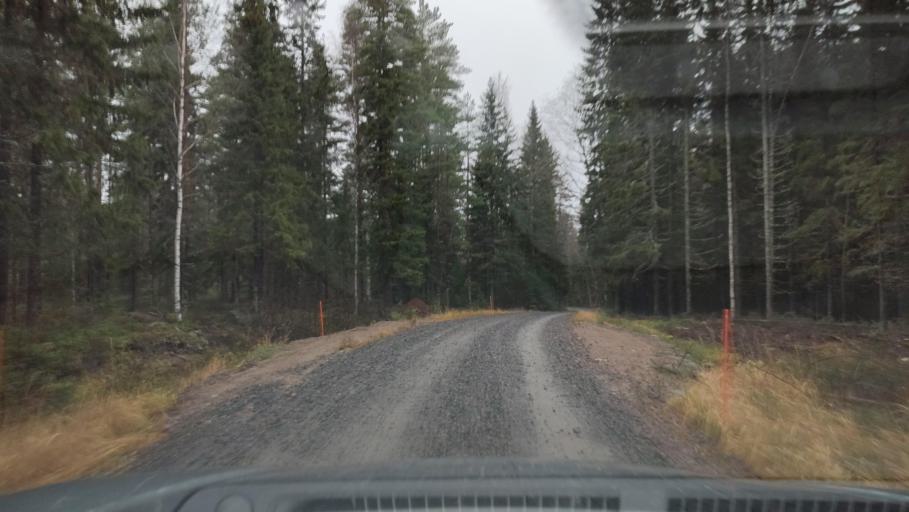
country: FI
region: Southern Ostrobothnia
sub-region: Suupohja
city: Karijoki
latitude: 62.1385
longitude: 21.6269
